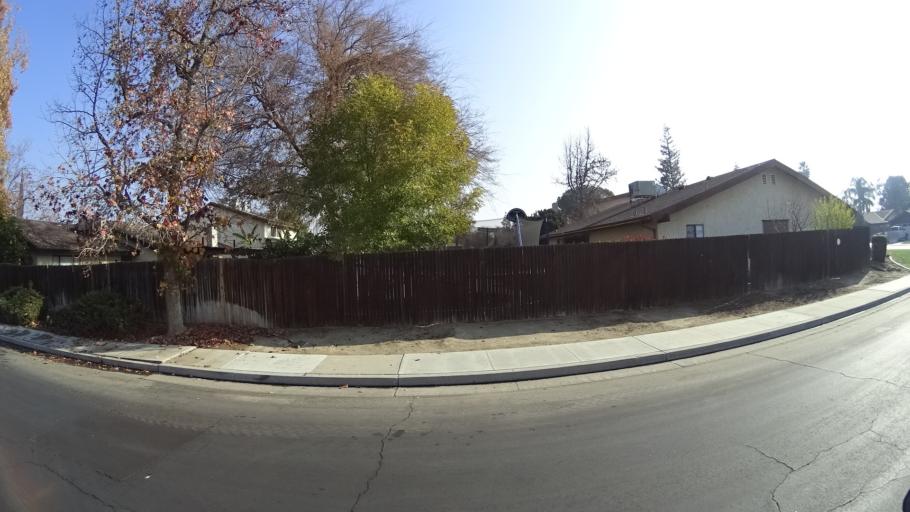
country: US
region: California
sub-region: Kern County
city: Greenacres
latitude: 35.3378
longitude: -119.0904
